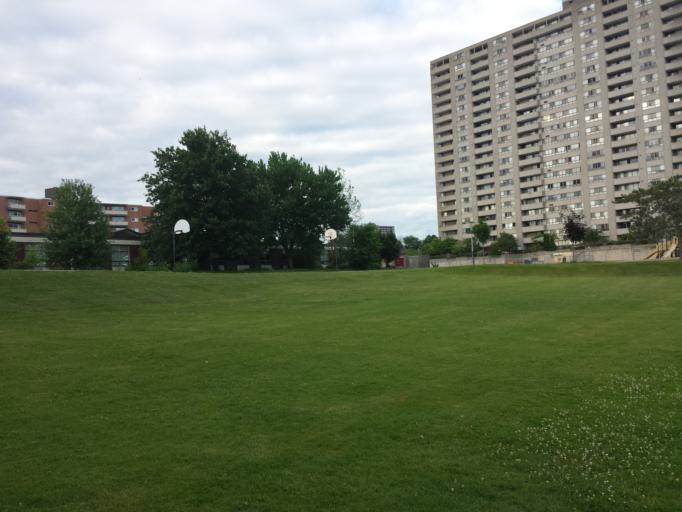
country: CA
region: Ontario
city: Bells Corners
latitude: 45.3675
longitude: -75.7904
